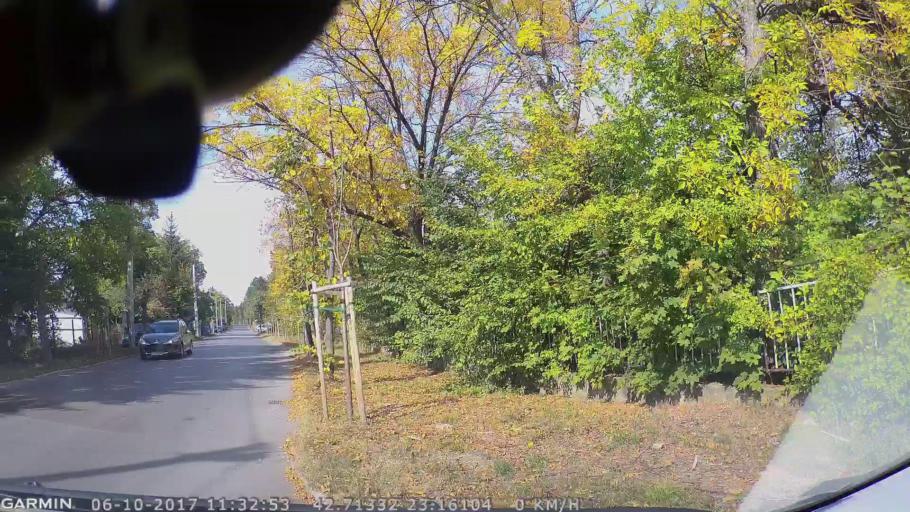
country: BG
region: Sofiya
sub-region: Obshtina Bozhurishte
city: Bozhurishte
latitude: 42.7121
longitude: 23.1586
